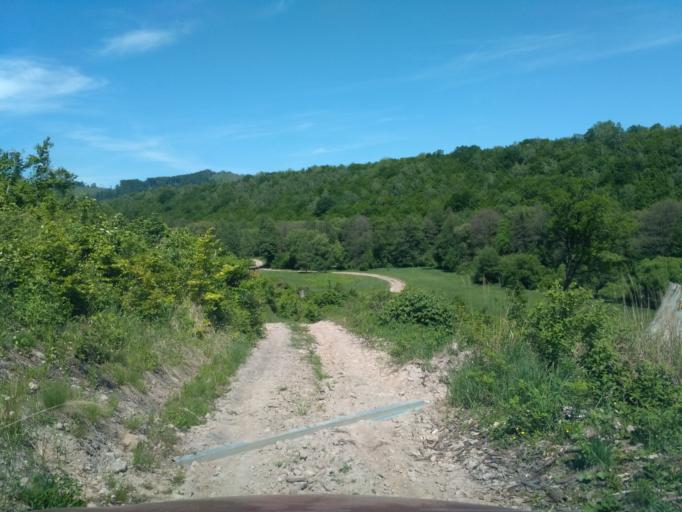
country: SK
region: Presovsky
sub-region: Okres Presov
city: Presov
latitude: 48.8827
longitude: 21.3940
